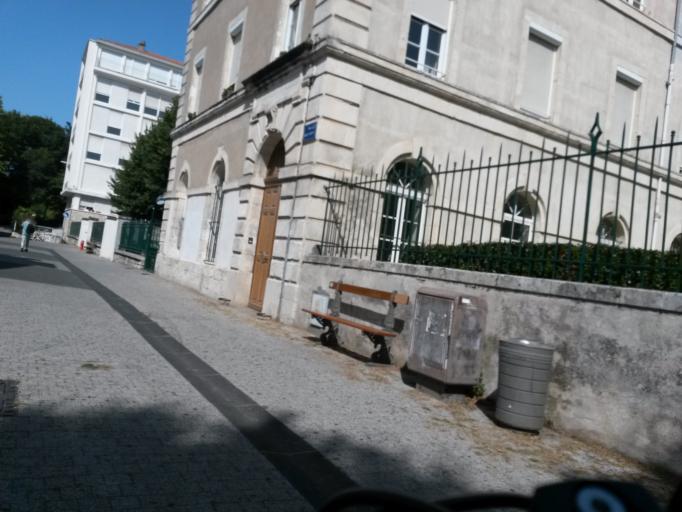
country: FR
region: Poitou-Charentes
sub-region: Departement de la Charente-Maritime
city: La Rochelle
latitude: 46.1646
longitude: -1.1545
